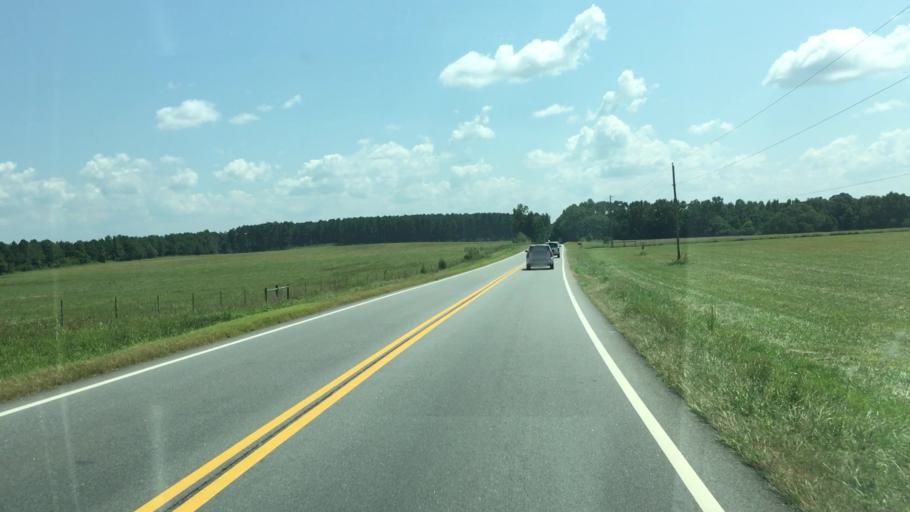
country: US
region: Georgia
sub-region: Oconee County
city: Watkinsville
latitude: 33.7977
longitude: -83.4255
